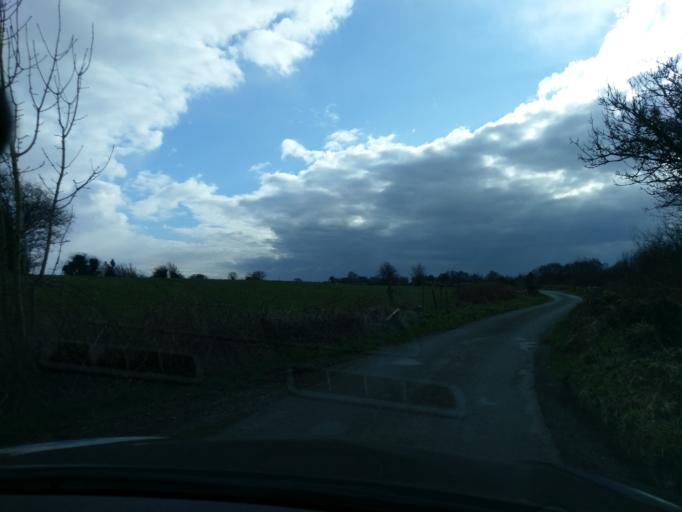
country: IE
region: Connaught
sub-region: County Galway
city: Athenry
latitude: 53.4454
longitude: -8.6549
